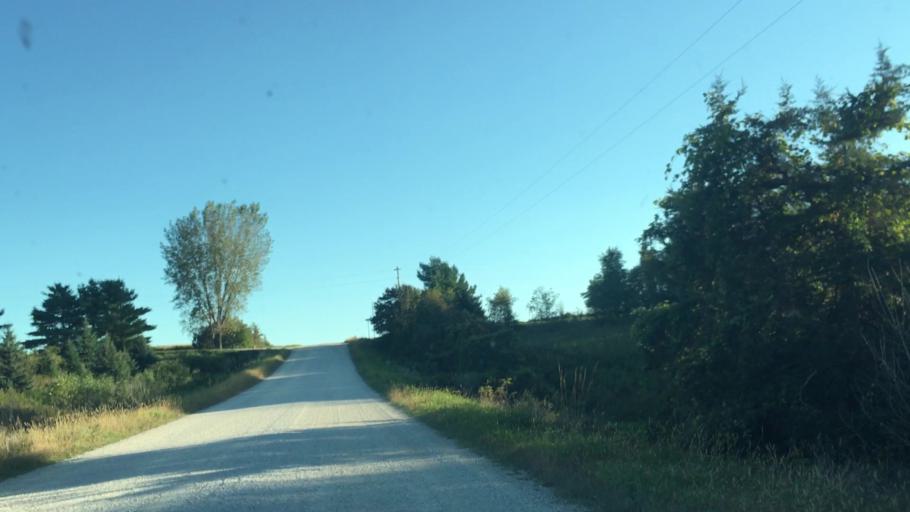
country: US
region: Minnesota
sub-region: Fillmore County
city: Preston
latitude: 43.7759
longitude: -92.0294
